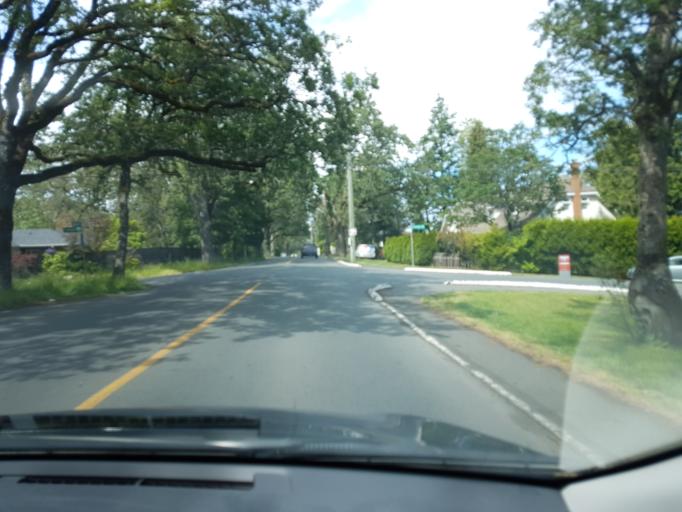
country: CA
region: British Columbia
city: Oak Bay
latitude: 48.4800
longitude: -123.3399
